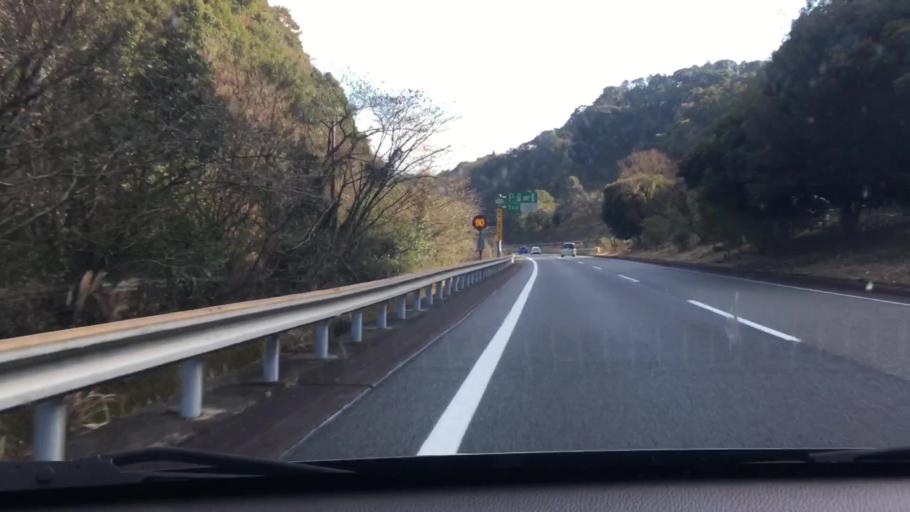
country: JP
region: Kumamoto
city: Hitoyoshi
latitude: 32.2702
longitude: 130.7603
